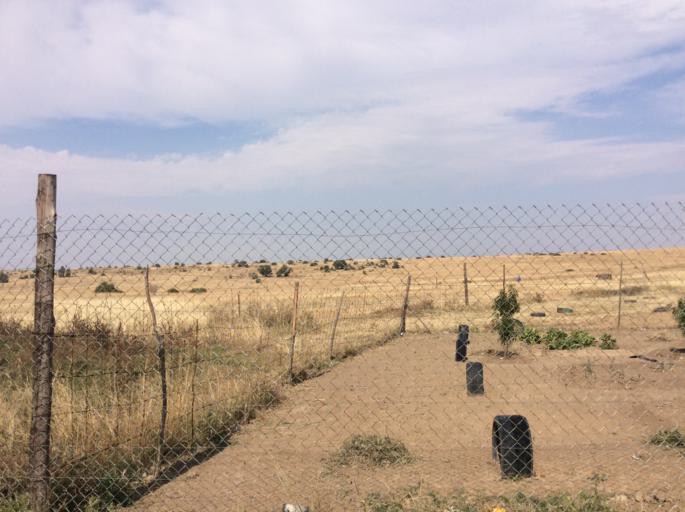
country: ZA
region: Orange Free State
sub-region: Xhariep District Municipality
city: Dewetsdorp
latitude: -29.5961
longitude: 26.6830
